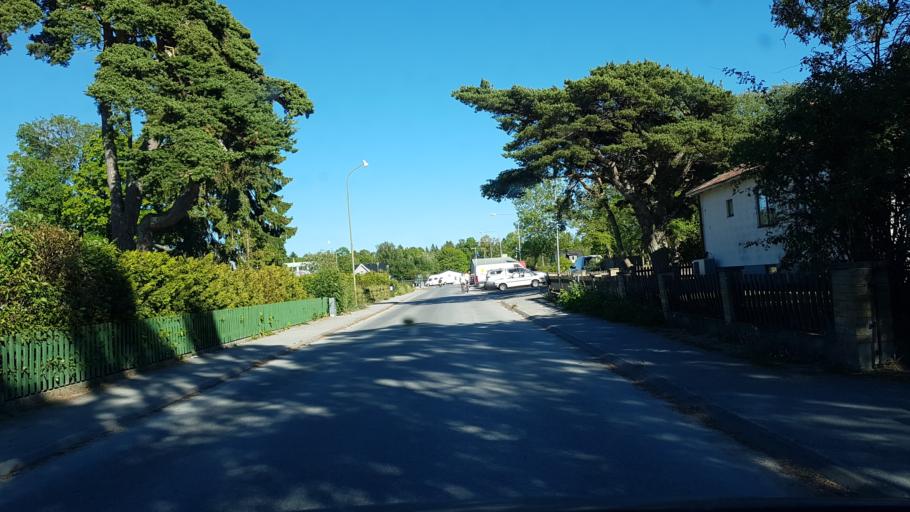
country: SE
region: Gotland
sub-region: Gotland
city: Vibble
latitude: 57.6016
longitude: 18.2489
